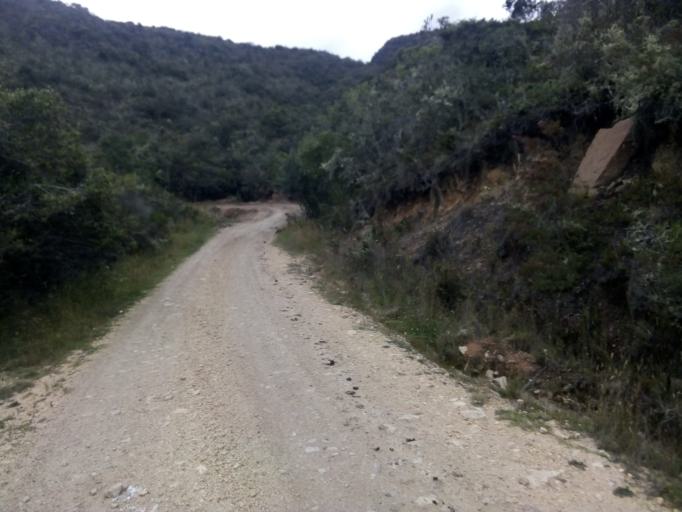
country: CO
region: Boyaca
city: Toca
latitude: 5.5868
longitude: -73.1269
